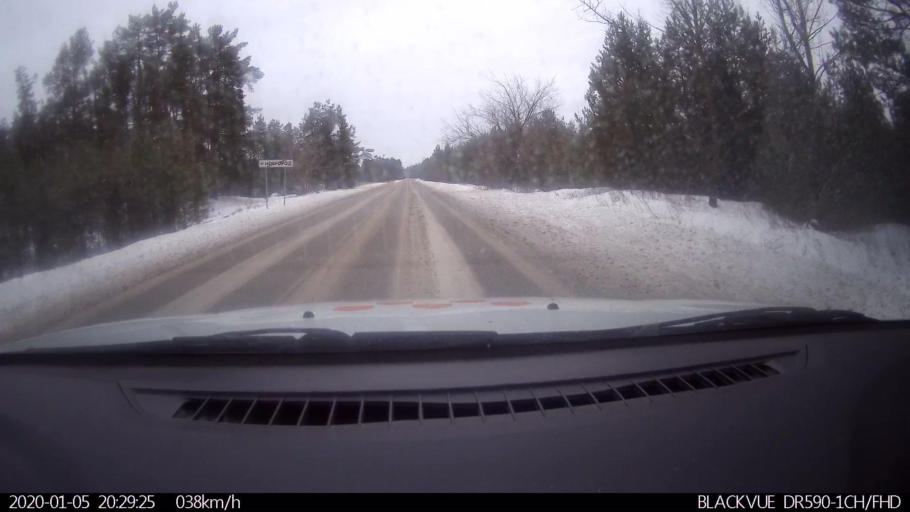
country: RU
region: Nizjnij Novgorod
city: Lukino
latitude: 56.3938
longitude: 43.7349
